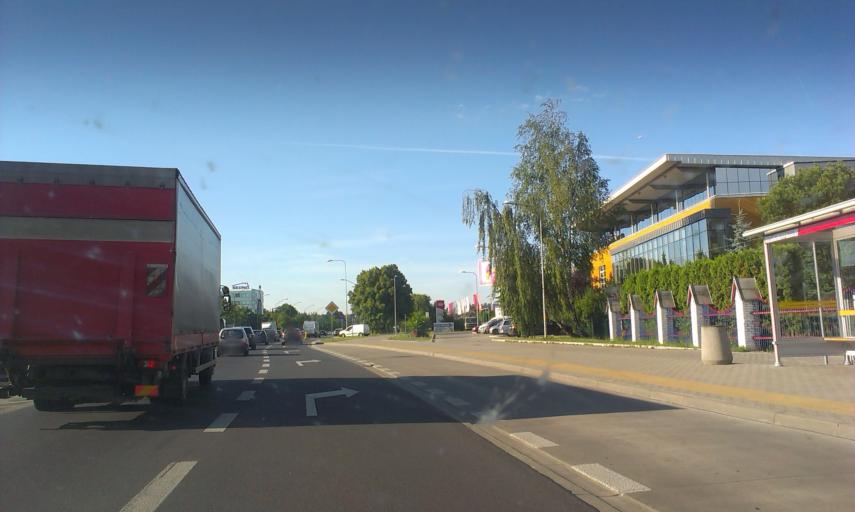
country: PL
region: Masovian Voivodeship
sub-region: Warszawa
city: Ursynow
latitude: 52.1388
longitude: 21.0174
